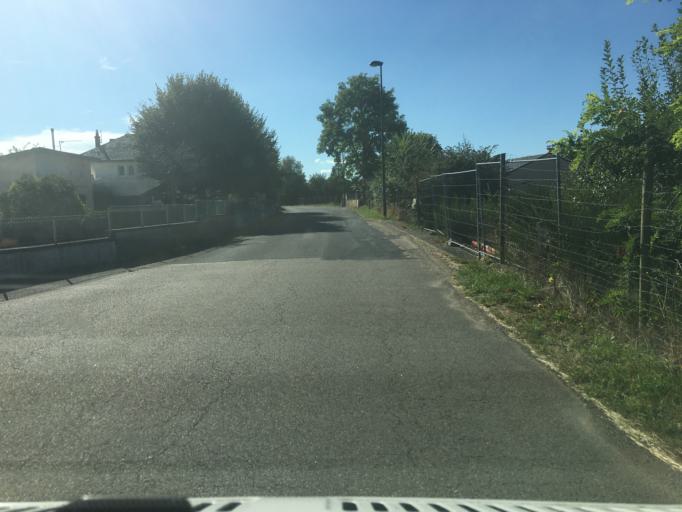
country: FR
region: Auvergne
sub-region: Departement du Cantal
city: Lanobre
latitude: 45.4404
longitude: 2.5260
